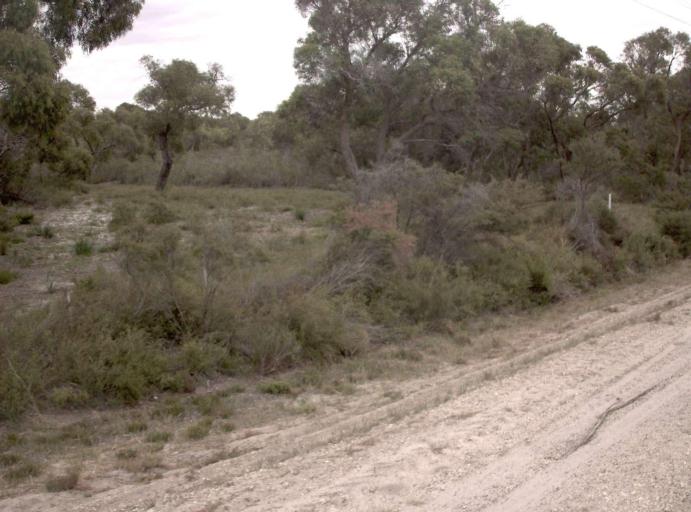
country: AU
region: Victoria
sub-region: Wellington
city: Sale
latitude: -38.1752
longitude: 147.3814
